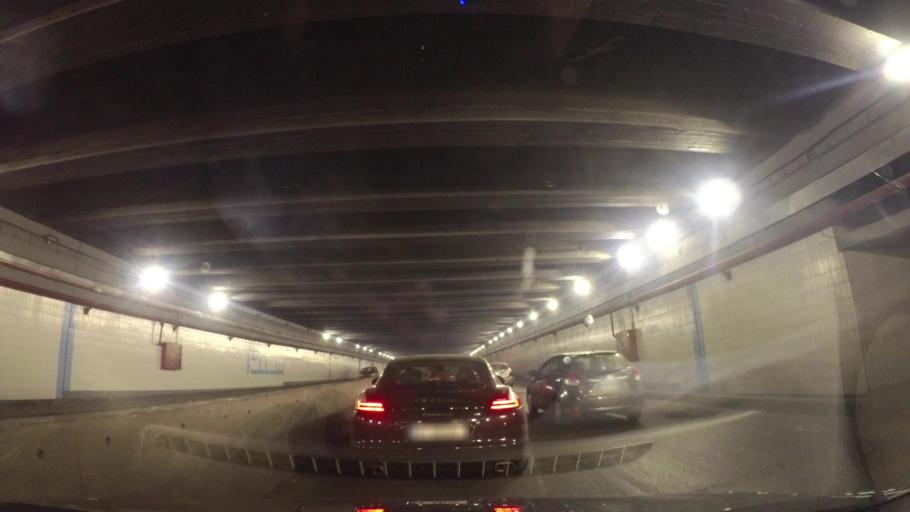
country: LB
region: Beyrouth
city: Beirut
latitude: 33.8839
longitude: 35.4972
